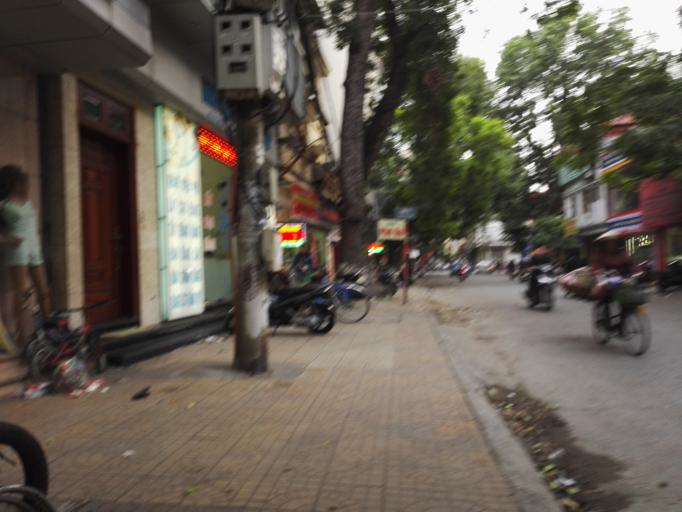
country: VN
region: Ha Noi
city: Hoan Kiem
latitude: 21.0470
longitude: 105.8471
